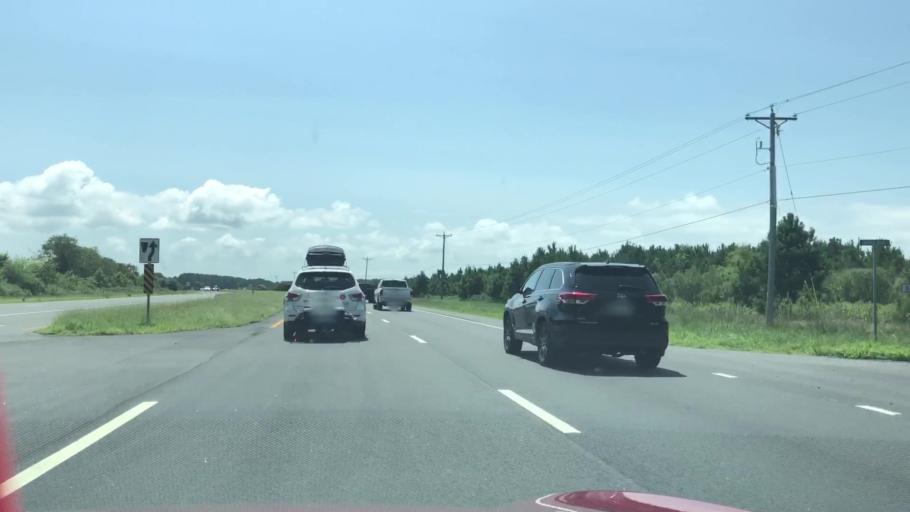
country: US
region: Virginia
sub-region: Northampton County
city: Cape Charles
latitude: 37.1465
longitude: -75.9713
